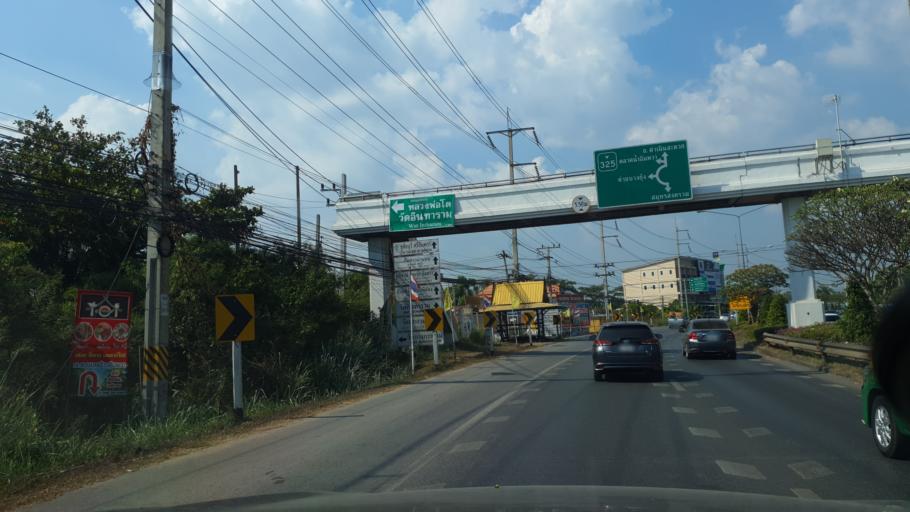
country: TH
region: Samut Songkhram
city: Amphawa
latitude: 13.4154
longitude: 99.9644
